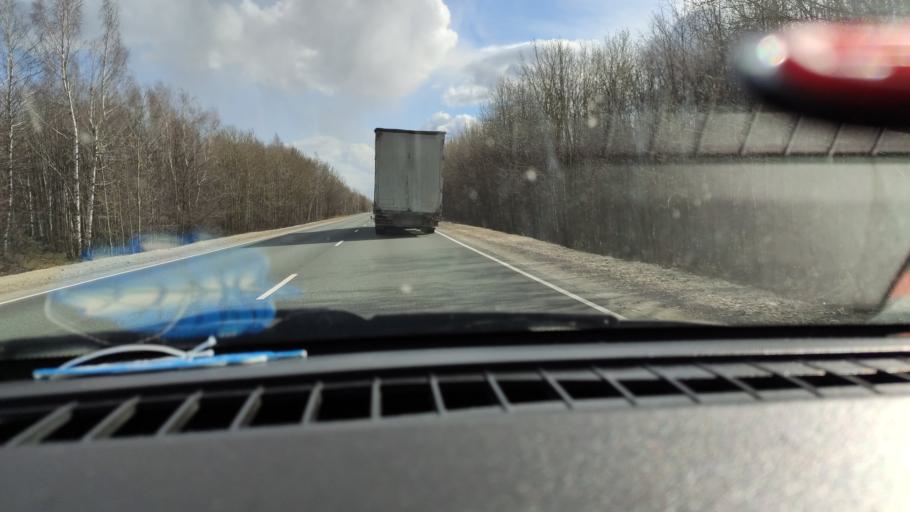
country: RU
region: Saratov
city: Khvalynsk
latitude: 52.4262
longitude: 48.0085
